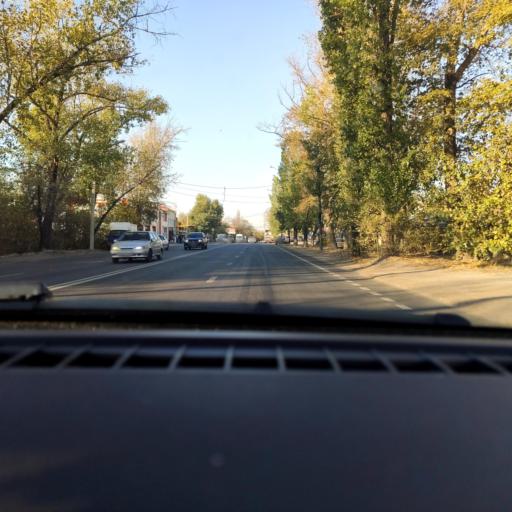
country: RU
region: Voronezj
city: Maslovka
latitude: 51.5969
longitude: 39.2521
